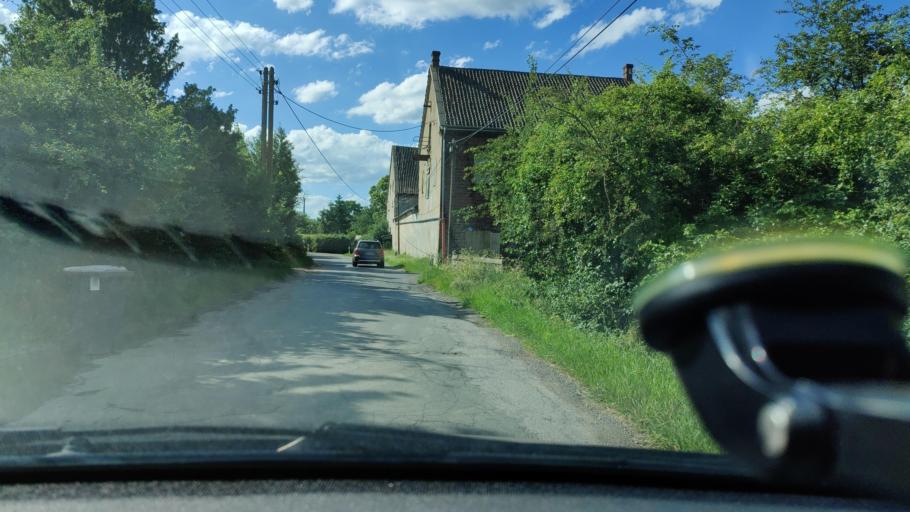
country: DE
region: North Rhine-Westphalia
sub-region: Regierungsbezirk Dusseldorf
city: Kamp-Lintfort
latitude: 51.5249
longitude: 6.5577
